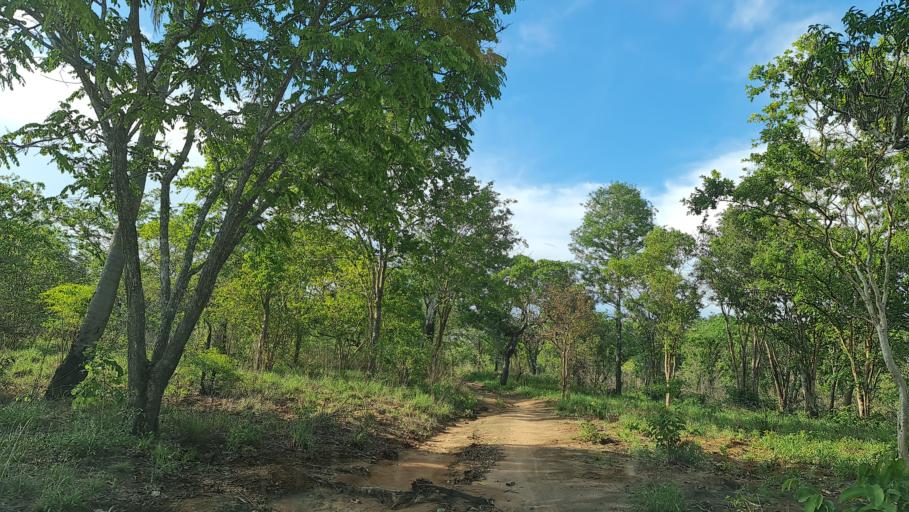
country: MZ
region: Zambezia
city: Quelimane
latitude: -17.1940
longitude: 37.4161
